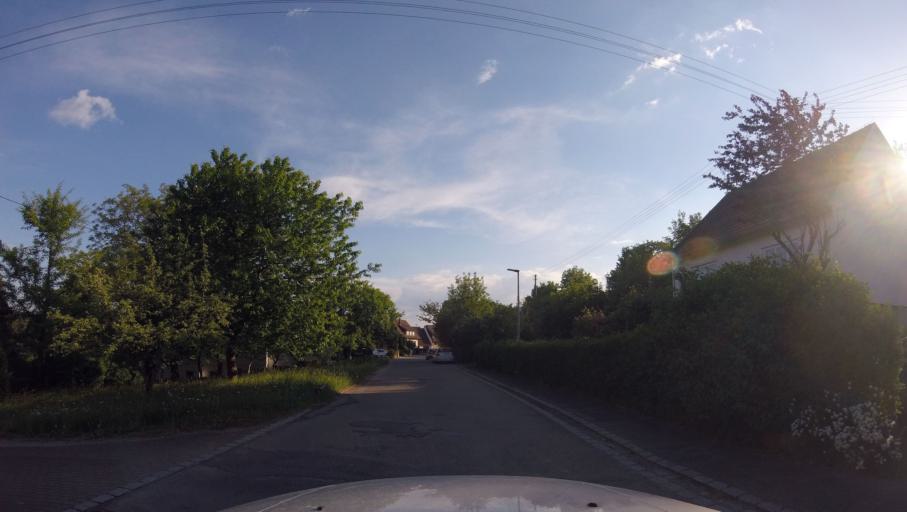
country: DE
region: Baden-Wuerttemberg
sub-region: Regierungsbezirk Stuttgart
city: Spiegelberg
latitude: 49.0316
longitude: 9.4127
